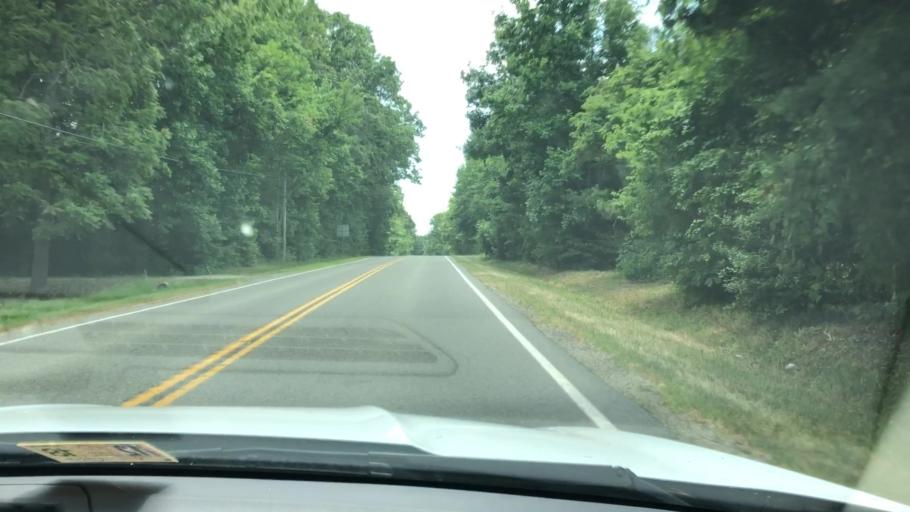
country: US
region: Virginia
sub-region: Lancaster County
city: Lancaster
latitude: 37.8365
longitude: -76.5774
